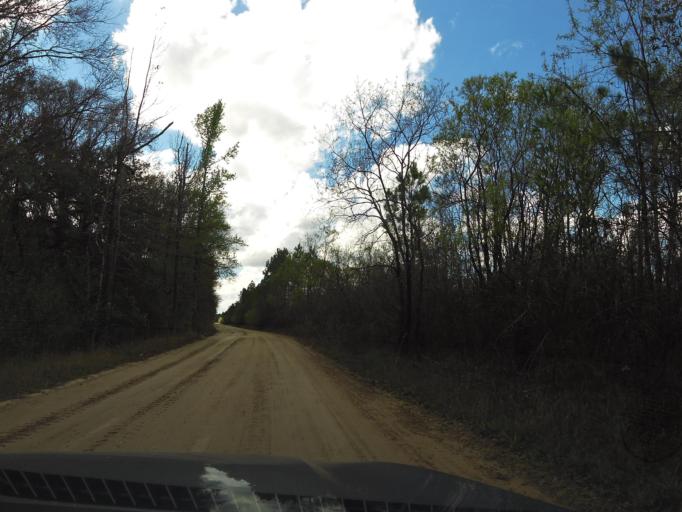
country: US
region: Florida
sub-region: Clay County
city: Green Cove Springs
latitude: 29.8609
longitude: -81.7177
